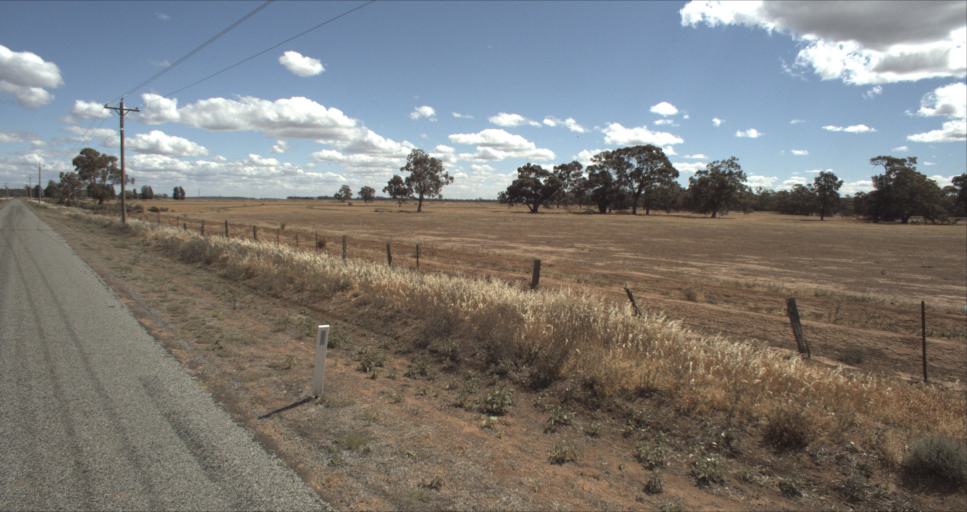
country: AU
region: New South Wales
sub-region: Leeton
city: Leeton
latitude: -34.5208
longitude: 146.2241
